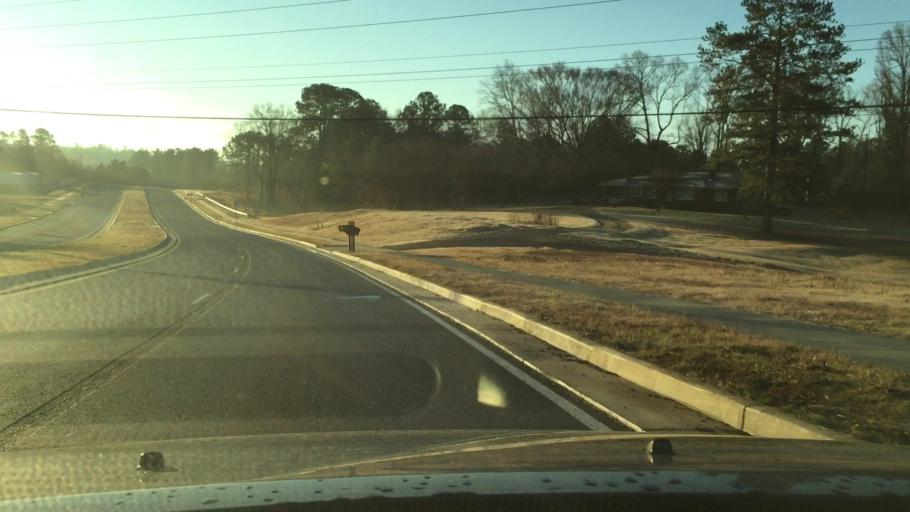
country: US
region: Georgia
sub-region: Forsyth County
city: Cumming
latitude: 34.1866
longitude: -84.1966
